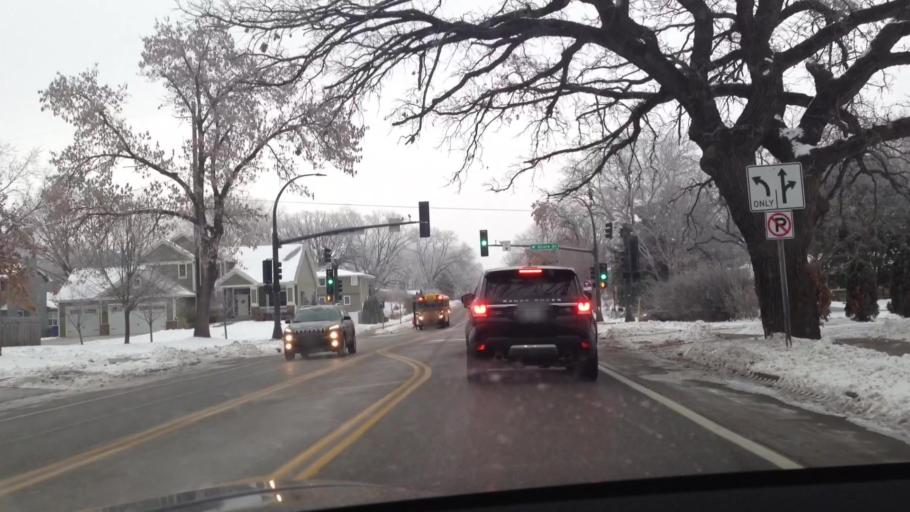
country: US
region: Minnesota
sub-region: Hennepin County
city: Edina
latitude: 44.8764
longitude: -93.3439
